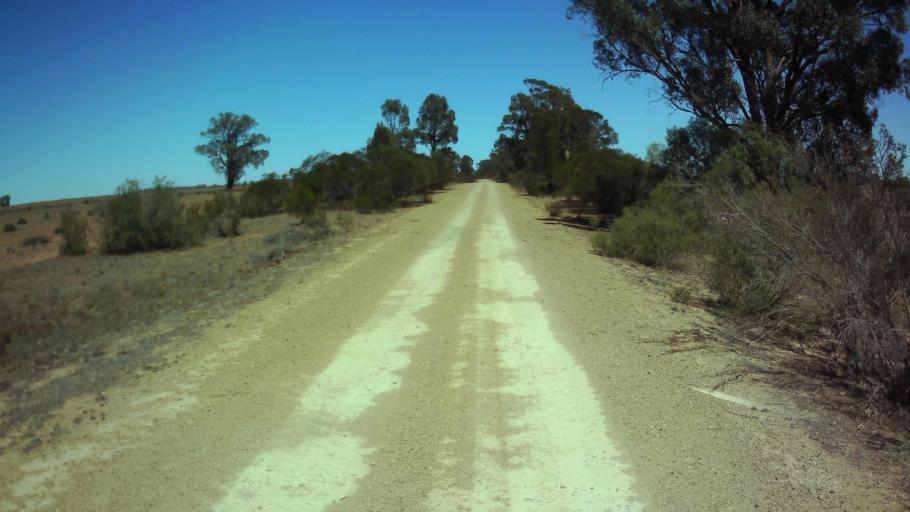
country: AU
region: New South Wales
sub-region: Forbes
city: Forbes
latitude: -33.6941
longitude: 147.8256
